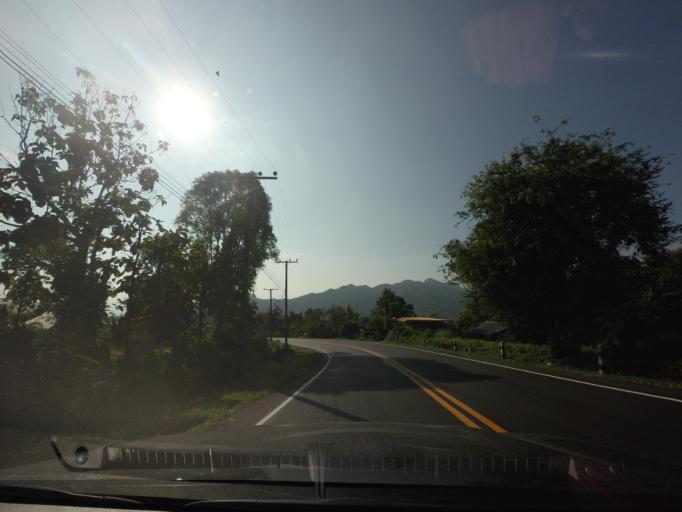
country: TH
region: Phetchabun
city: Lom Kao
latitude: 16.8745
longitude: 101.1306
